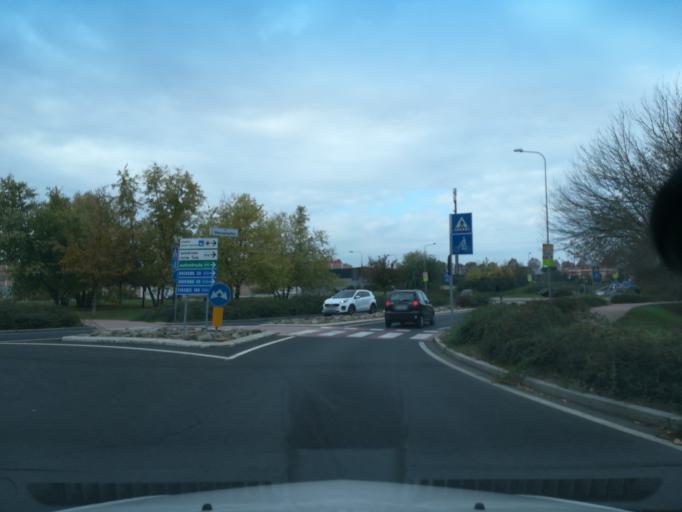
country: IT
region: Emilia-Romagna
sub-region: Provincia di Bologna
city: Imola
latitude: 44.3629
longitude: 11.7015
